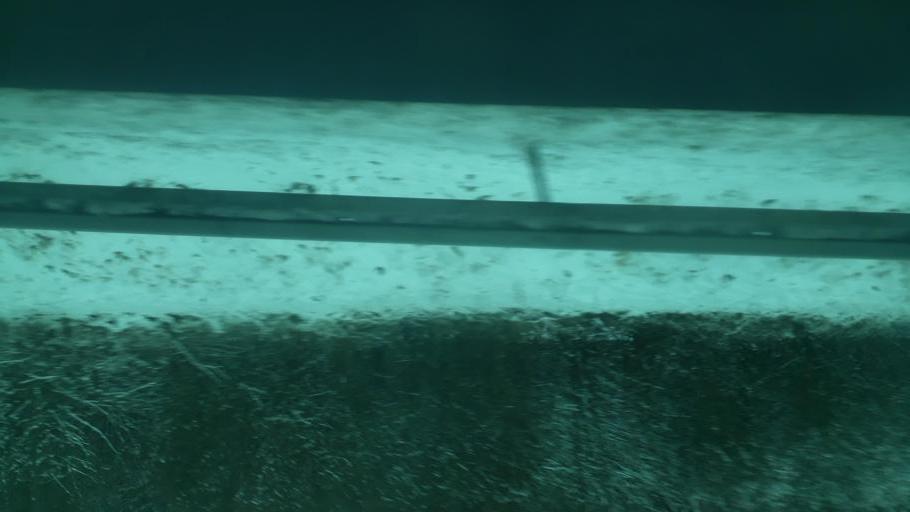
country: DE
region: Bavaria
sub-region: Upper Palatinate
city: Pleystein
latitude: 49.6260
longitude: 12.4351
